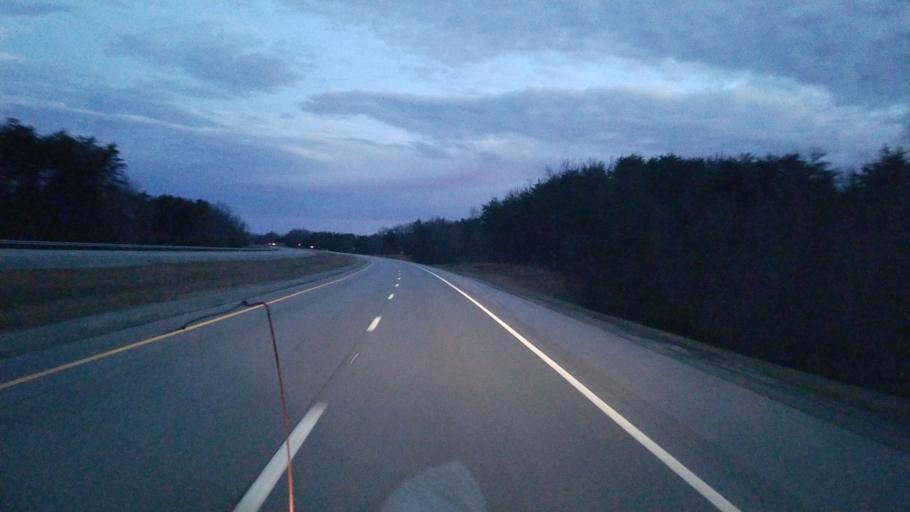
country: US
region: Tennessee
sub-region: Van Buren County
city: Spencer
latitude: 35.6023
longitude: -85.4684
